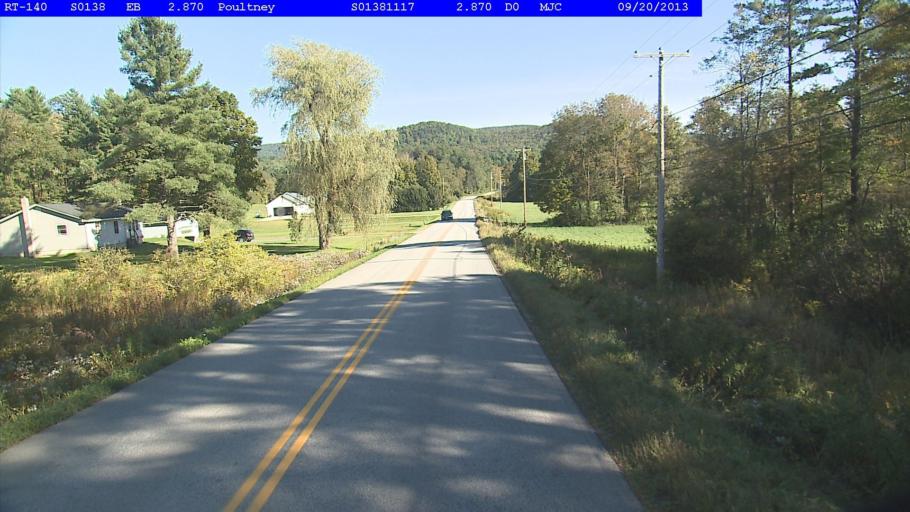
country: US
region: Vermont
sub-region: Rutland County
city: Poultney
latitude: 43.5226
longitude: -73.1827
